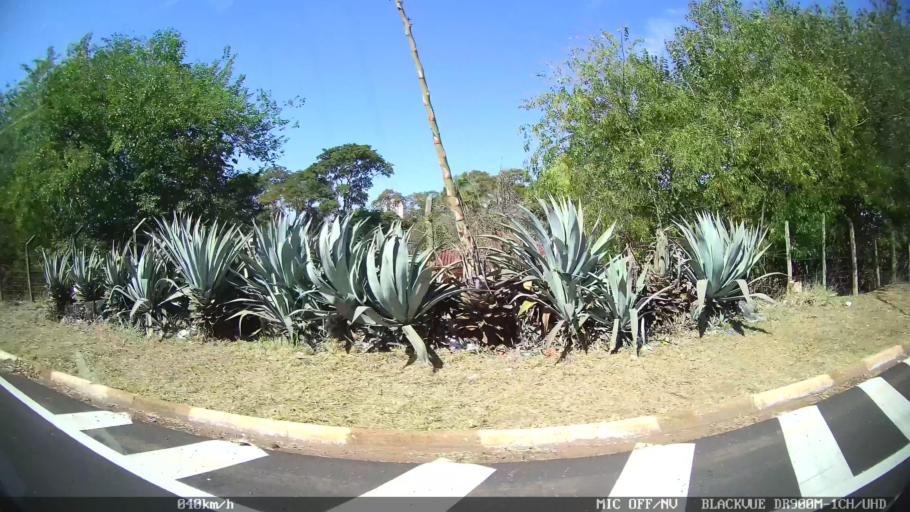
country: BR
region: Sao Paulo
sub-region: Franca
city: Franca
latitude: -20.5450
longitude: -47.4235
